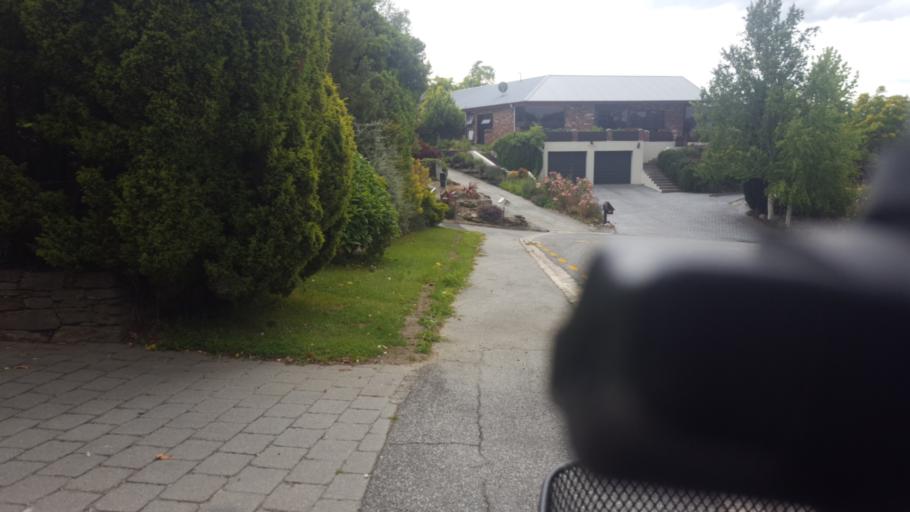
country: NZ
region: Otago
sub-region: Queenstown-Lakes District
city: Wanaka
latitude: -45.2607
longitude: 169.3814
